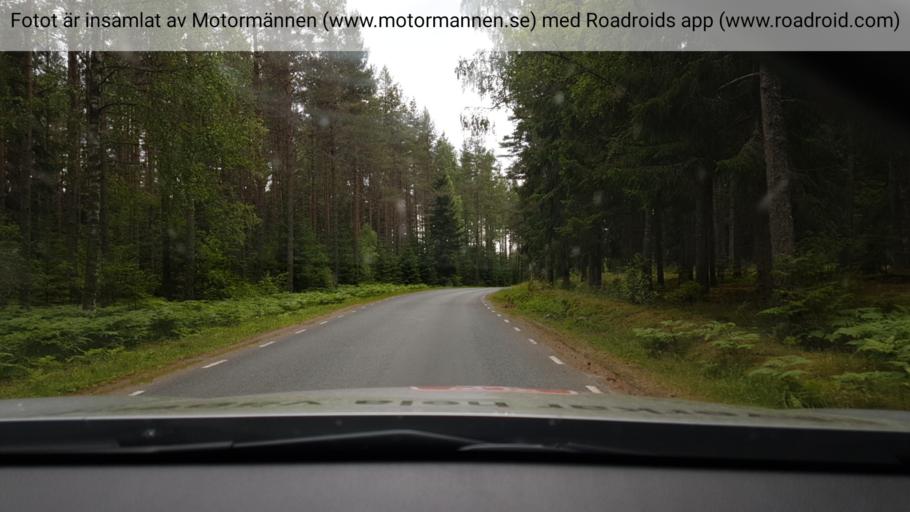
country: SE
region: Joenkoeping
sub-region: Habo Kommun
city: Habo
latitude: 57.9987
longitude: 14.0089
